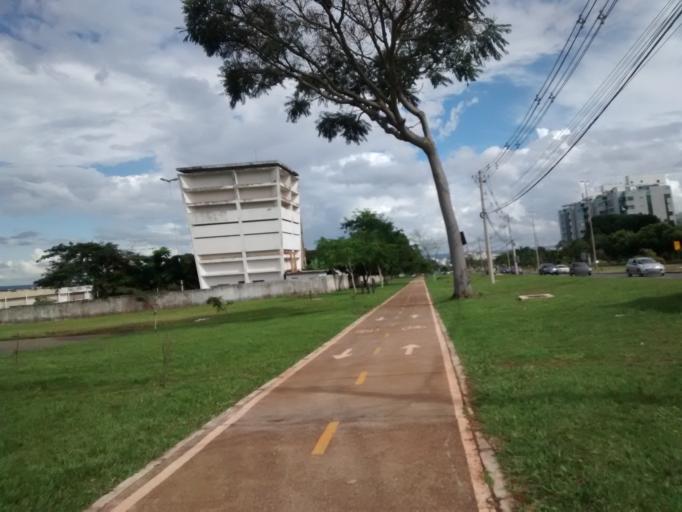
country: BR
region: Federal District
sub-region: Brasilia
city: Brasilia
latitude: -15.7893
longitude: -47.9151
